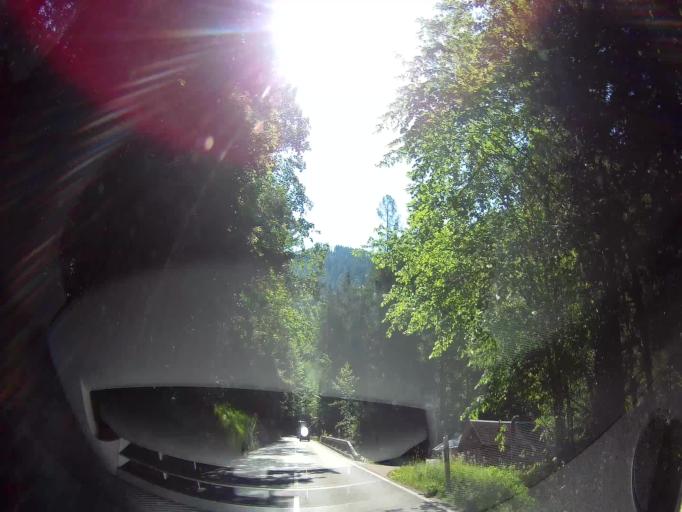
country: AT
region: Salzburg
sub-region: Politischer Bezirk Hallein
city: Hallein
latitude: 47.6424
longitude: 13.0607
